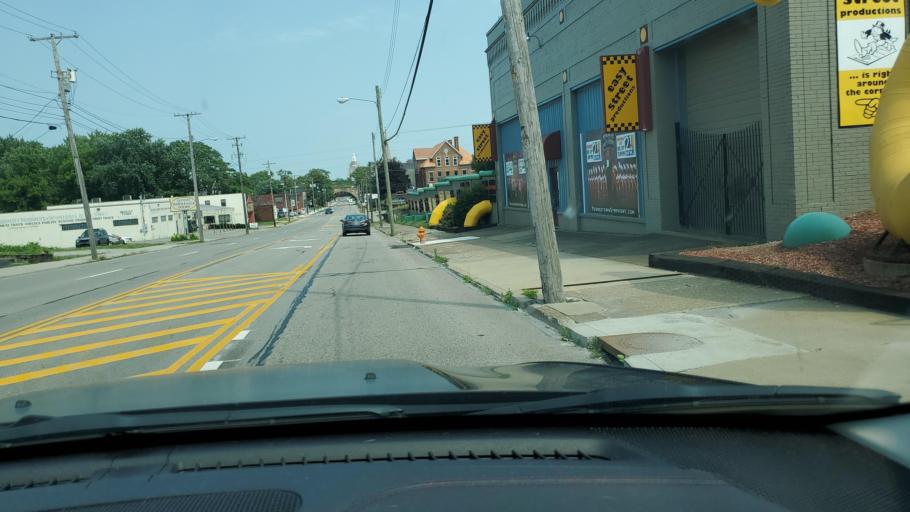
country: US
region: Ohio
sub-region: Mahoning County
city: Youngstown
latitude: 41.1017
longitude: -80.6666
